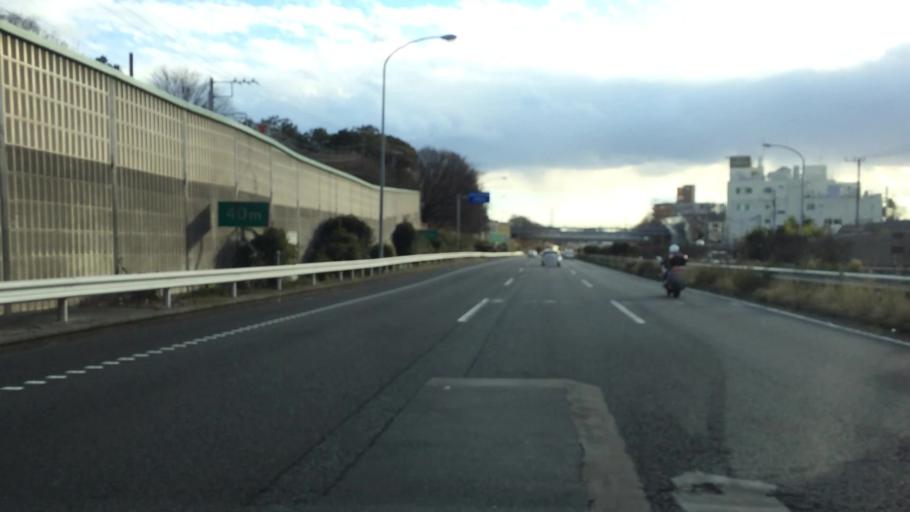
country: JP
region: Tokyo
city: Chofugaoka
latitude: 35.5779
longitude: 139.6173
